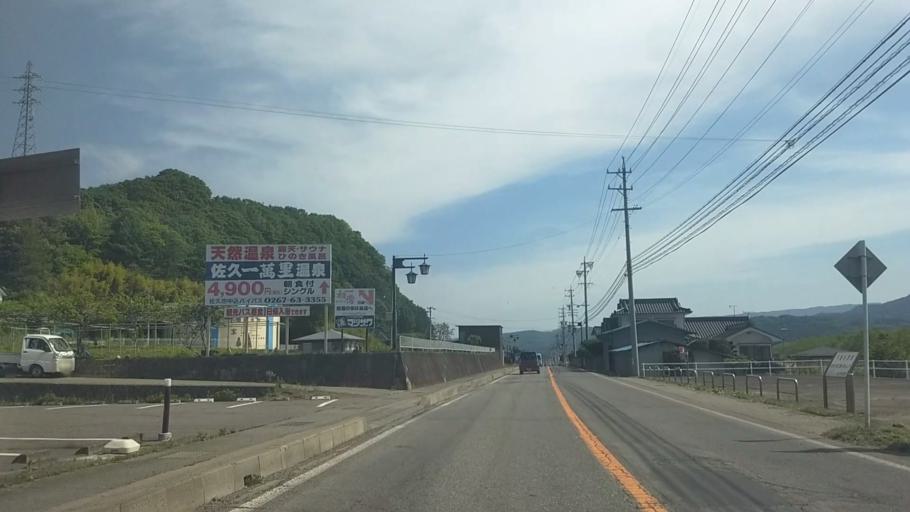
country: JP
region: Nagano
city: Saku
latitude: 36.1531
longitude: 138.4761
